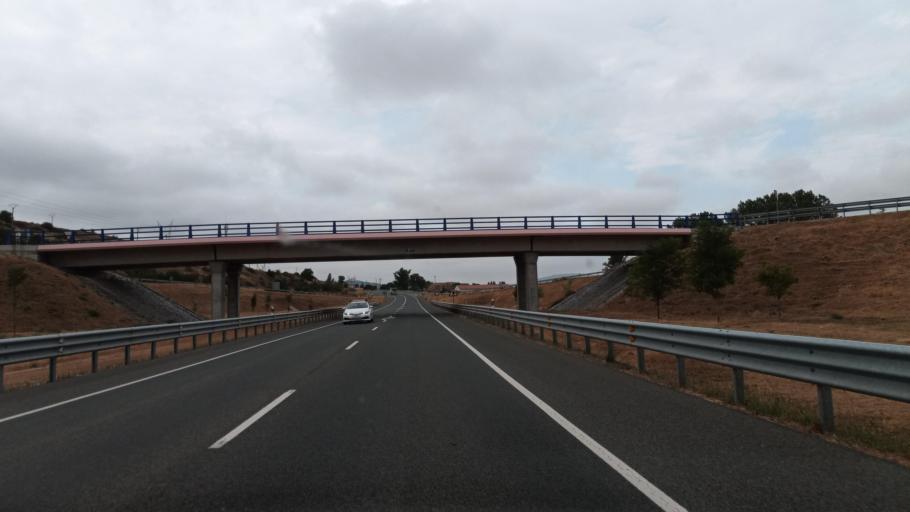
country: ES
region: Castille and Leon
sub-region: Provincia de Burgos
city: Castil de Peones
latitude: 42.4876
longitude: -3.3752
